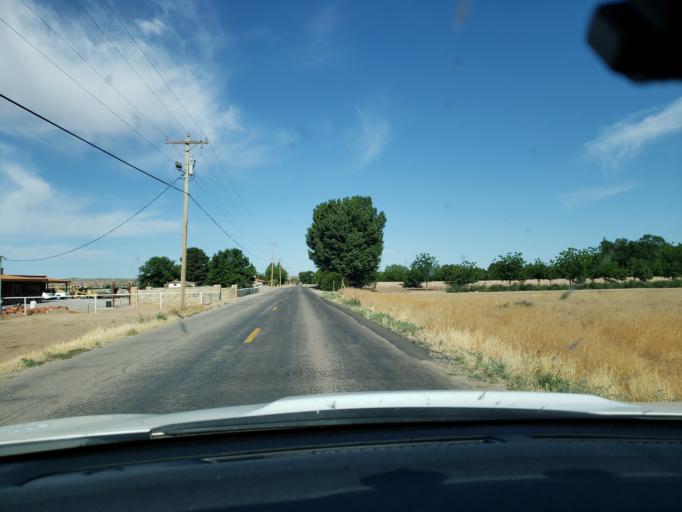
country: US
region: New Mexico
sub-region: Dona Ana County
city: Vado
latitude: 32.0826
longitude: -106.6852
